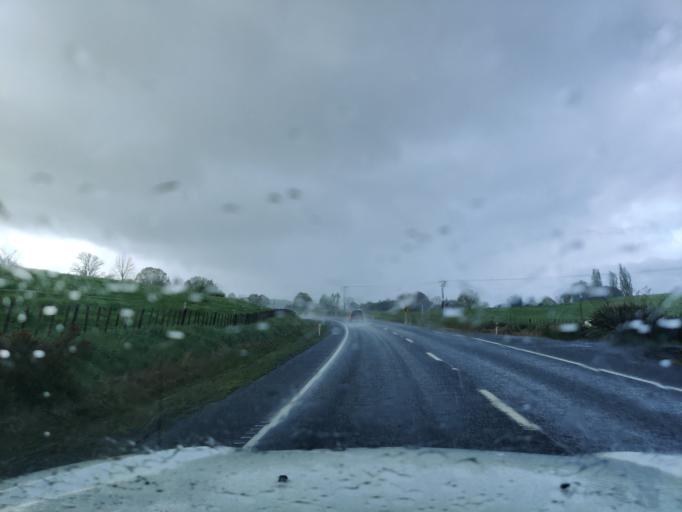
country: NZ
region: Waikato
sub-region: Matamata-Piako District
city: Matamata
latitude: -37.9828
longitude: 175.7046
